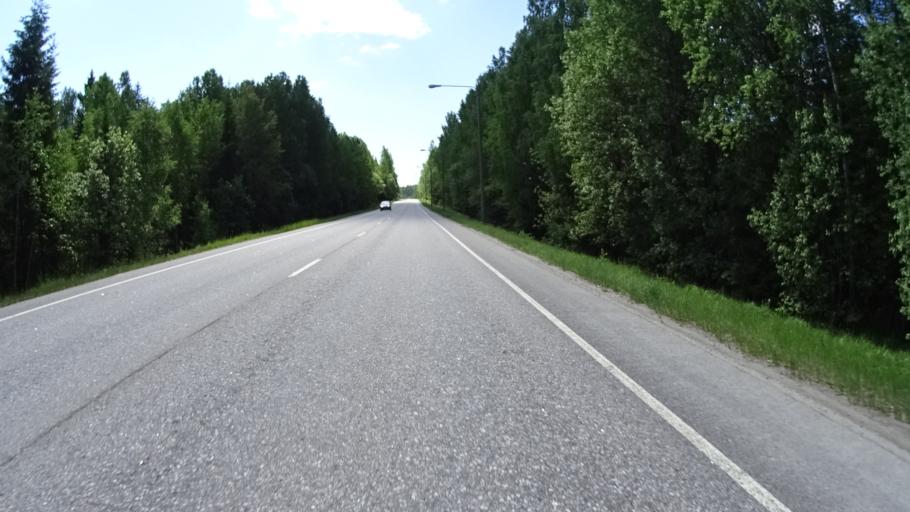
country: FI
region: Uusimaa
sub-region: Helsinki
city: Nurmijaervi
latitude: 60.3783
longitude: 24.8065
